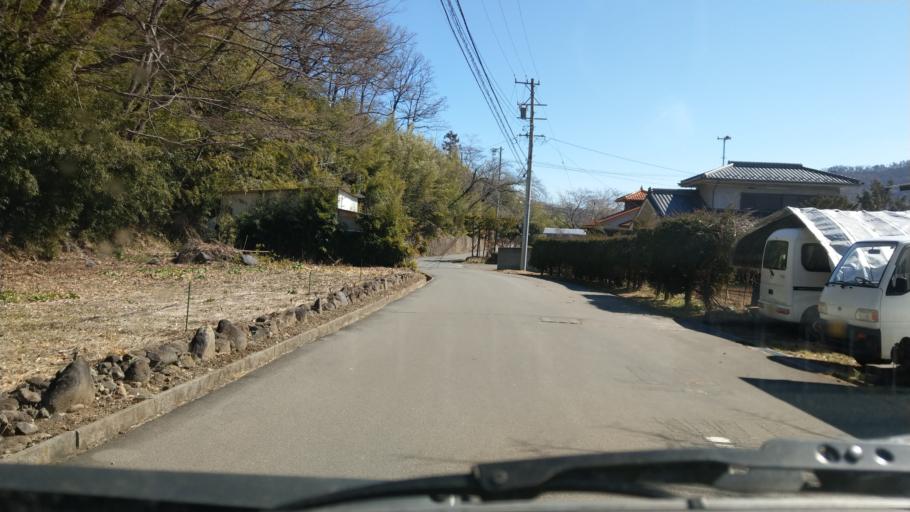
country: JP
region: Nagano
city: Komoro
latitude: 36.3346
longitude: 138.3949
